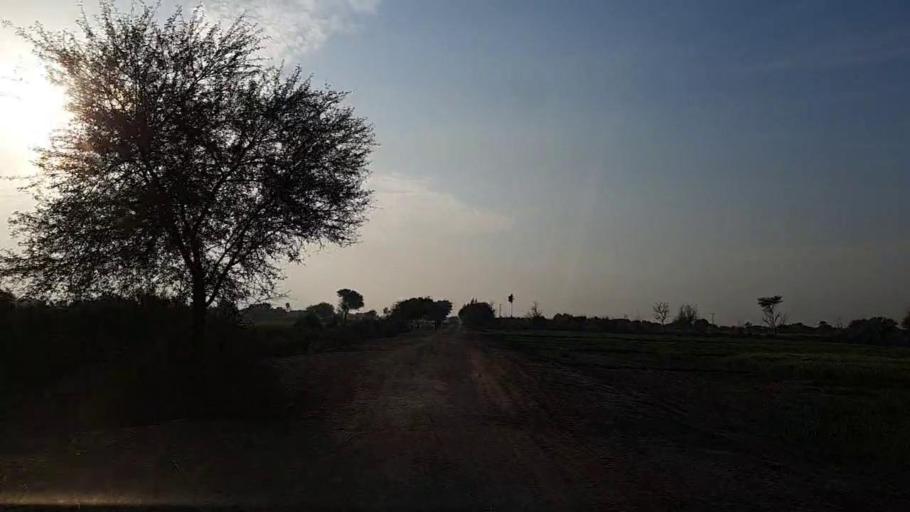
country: PK
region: Sindh
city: Jam Sahib
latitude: 26.3953
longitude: 68.5366
